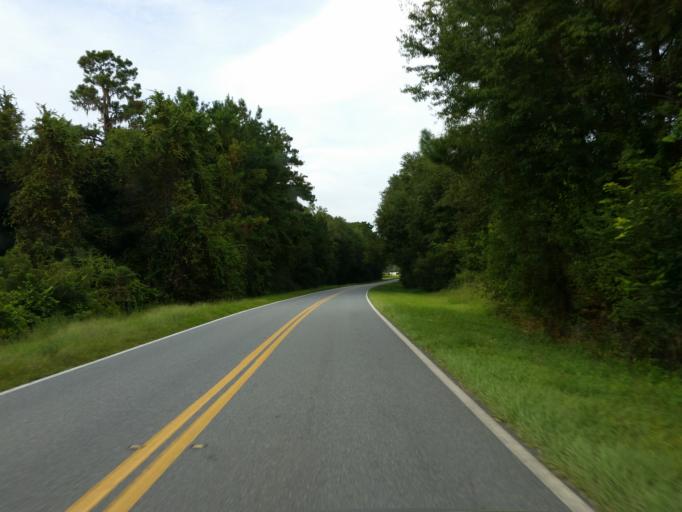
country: US
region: Georgia
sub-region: Echols County
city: Statenville
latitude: 30.5510
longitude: -83.1887
